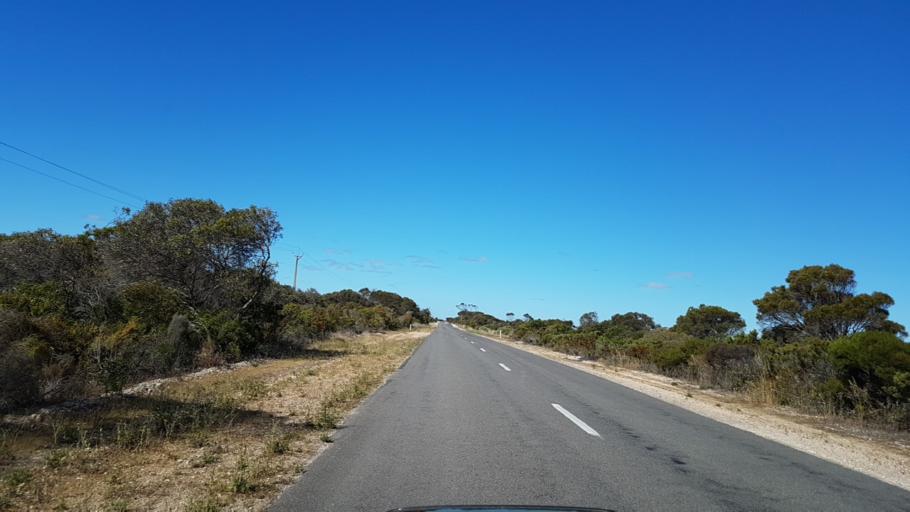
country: AU
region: South Australia
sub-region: Yorke Peninsula
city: Honiton
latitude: -35.1209
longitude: 137.1243
